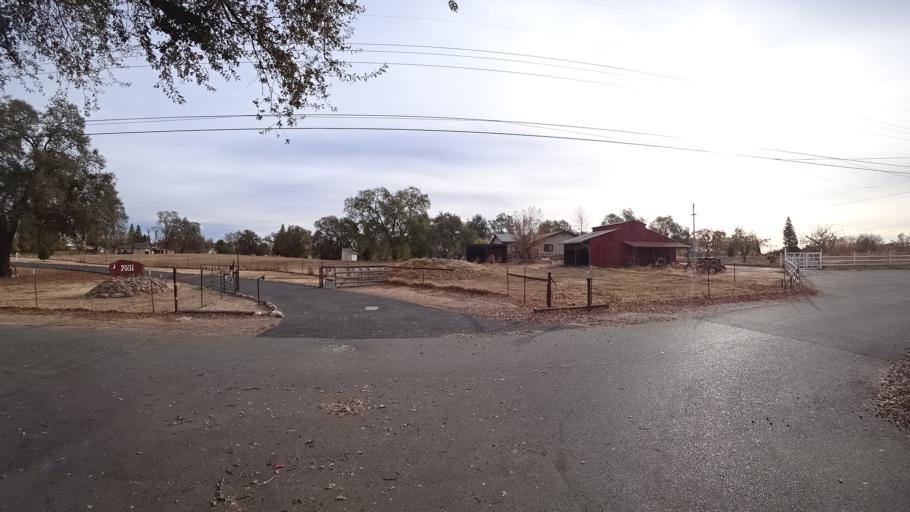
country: US
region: California
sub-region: Sacramento County
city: Citrus Heights
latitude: 38.7203
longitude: -121.2837
